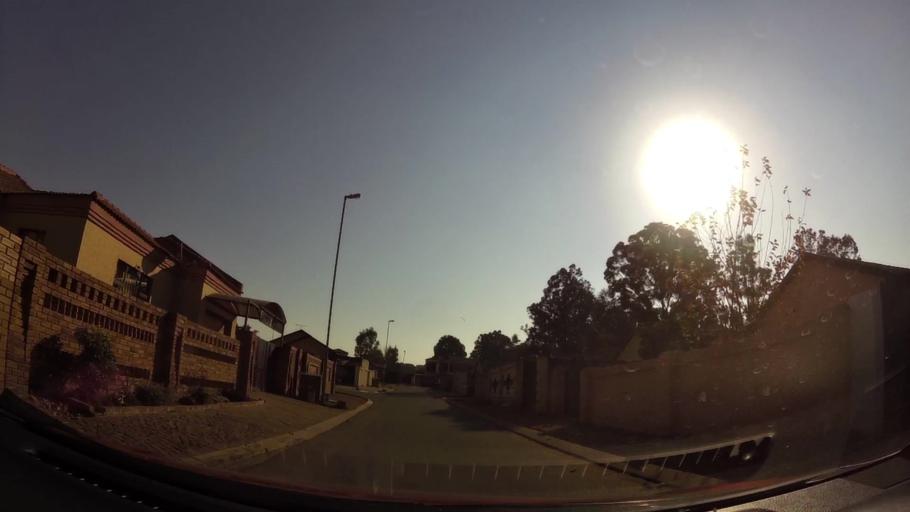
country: ZA
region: Gauteng
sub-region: City of Johannesburg Metropolitan Municipality
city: Soweto
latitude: -26.2971
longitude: 27.9528
